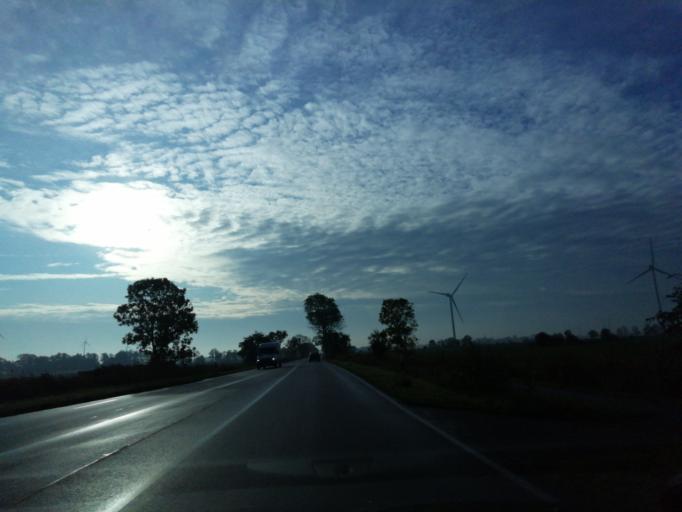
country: DE
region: Lower Saxony
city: Fedderwarden
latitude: 53.6149
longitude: 8.0390
